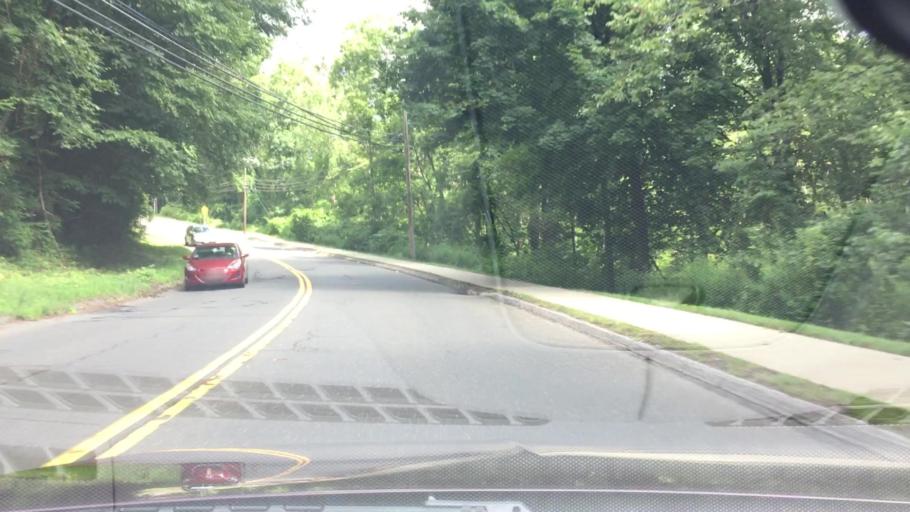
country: US
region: Connecticut
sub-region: Fairfield County
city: Danbury
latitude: 41.4315
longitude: -73.4248
